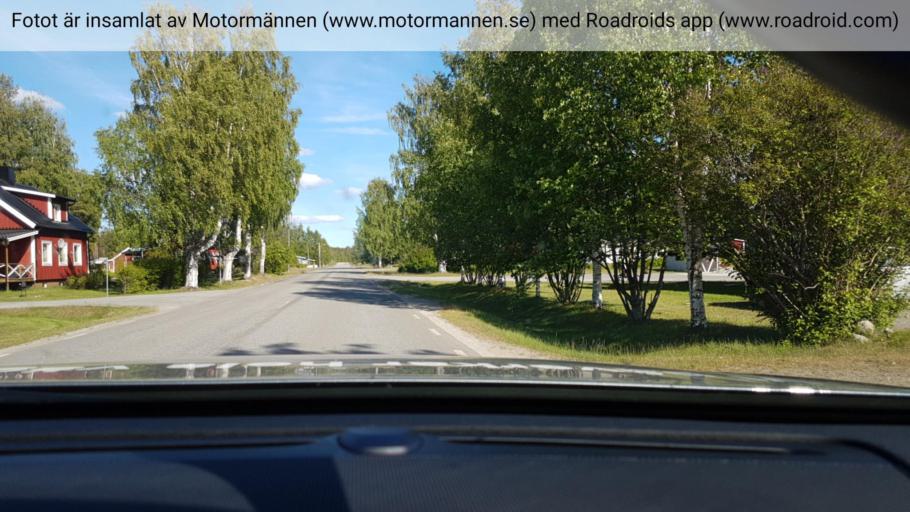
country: SE
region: Vaesterbotten
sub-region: Lycksele Kommun
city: Lycksele
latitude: 64.8138
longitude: 18.9008
